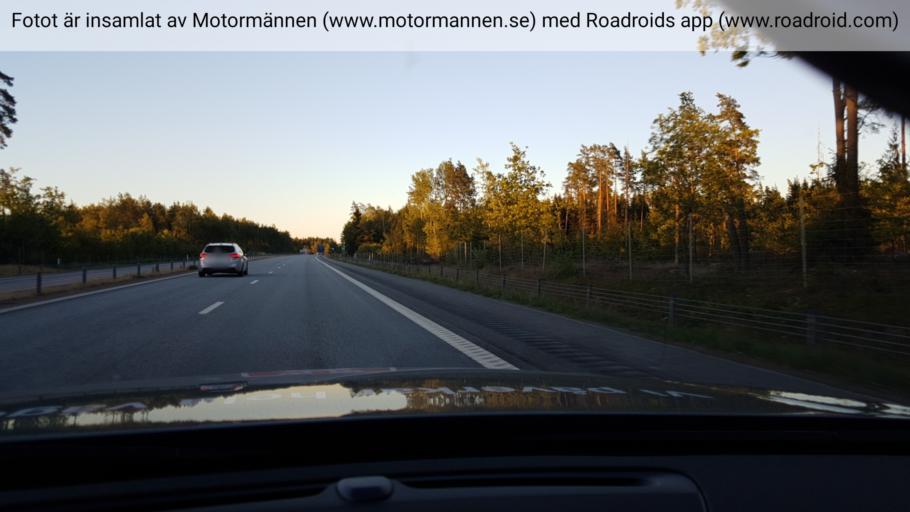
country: SE
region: Vaestmanland
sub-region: Hallstahammars Kommun
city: Kolback
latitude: 59.5845
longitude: 16.3718
